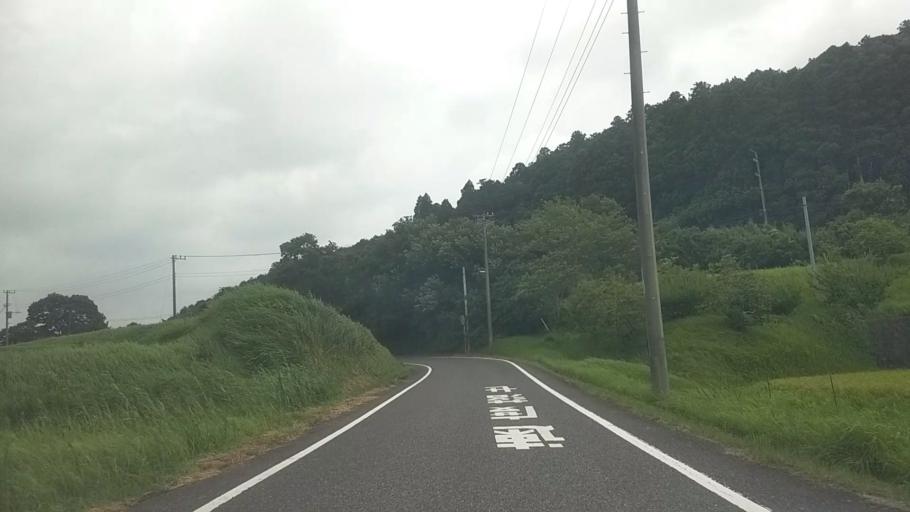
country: JP
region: Chiba
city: Kawaguchi
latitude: 35.2619
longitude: 140.0577
